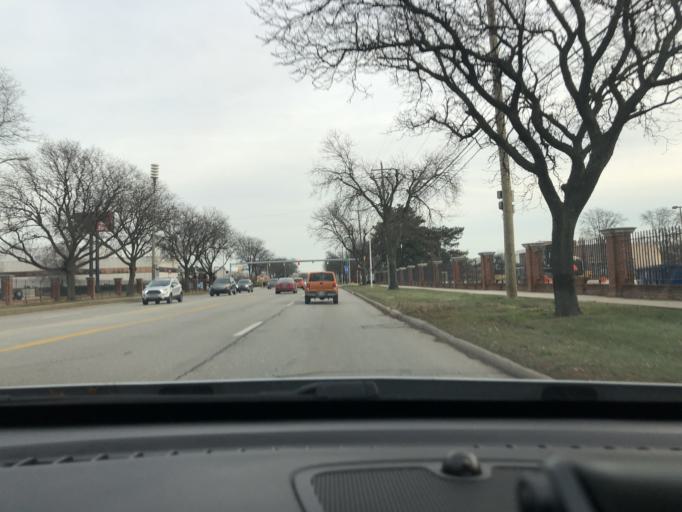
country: US
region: Michigan
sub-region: Wayne County
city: Allen Park
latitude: 42.3009
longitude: -83.2354
